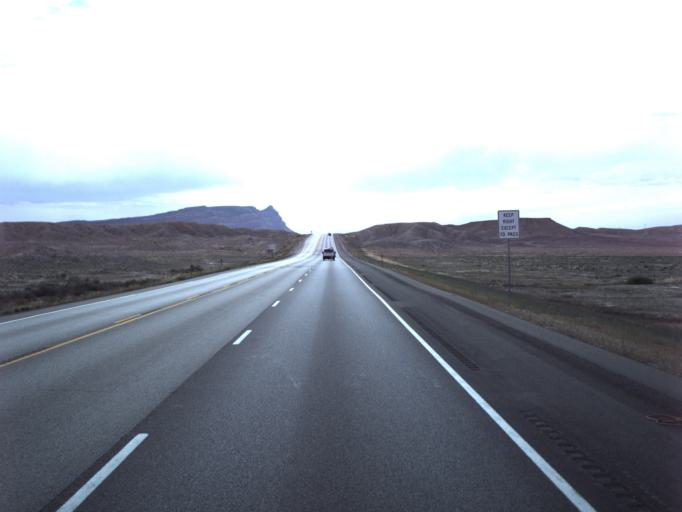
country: US
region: Utah
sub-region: Carbon County
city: East Carbon City
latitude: 39.3108
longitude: -110.3610
